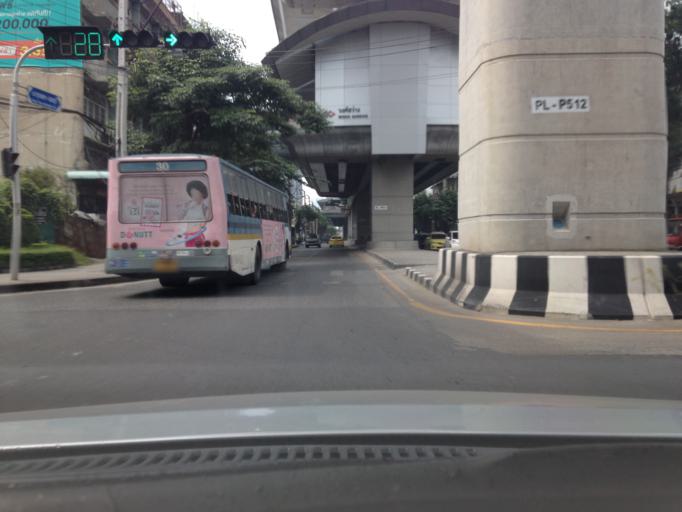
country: TH
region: Bangkok
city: Bang Sue
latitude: 13.8280
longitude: 100.5285
